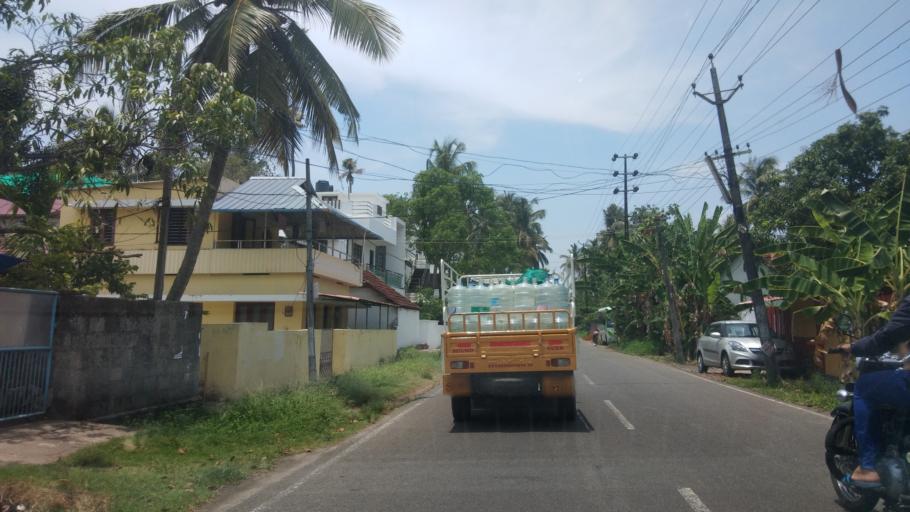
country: IN
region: Kerala
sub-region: Alappuzha
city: Kutiatodu
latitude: 9.8506
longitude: 76.2667
